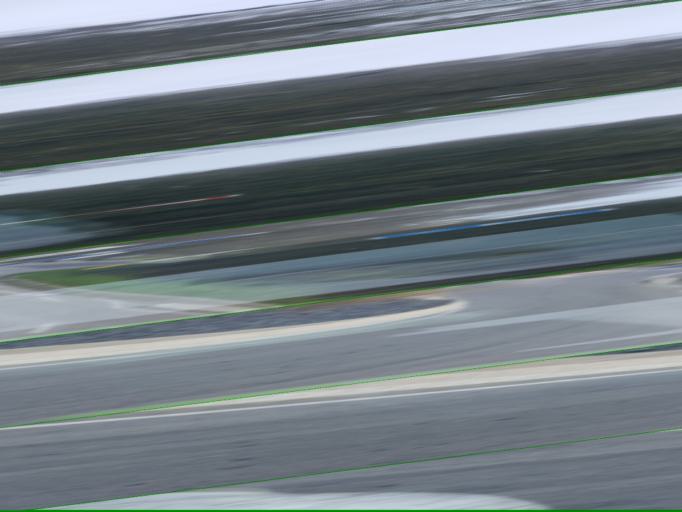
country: FR
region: Ile-de-France
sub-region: Departement des Yvelines
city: Houdan
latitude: 48.7922
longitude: 1.5933
